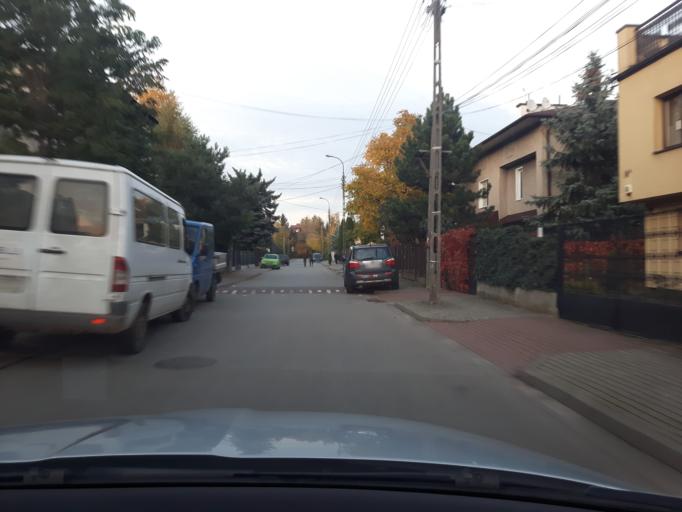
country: PL
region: Masovian Voivodeship
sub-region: Warszawa
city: Targowek
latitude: 52.2813
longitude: 21.0723
